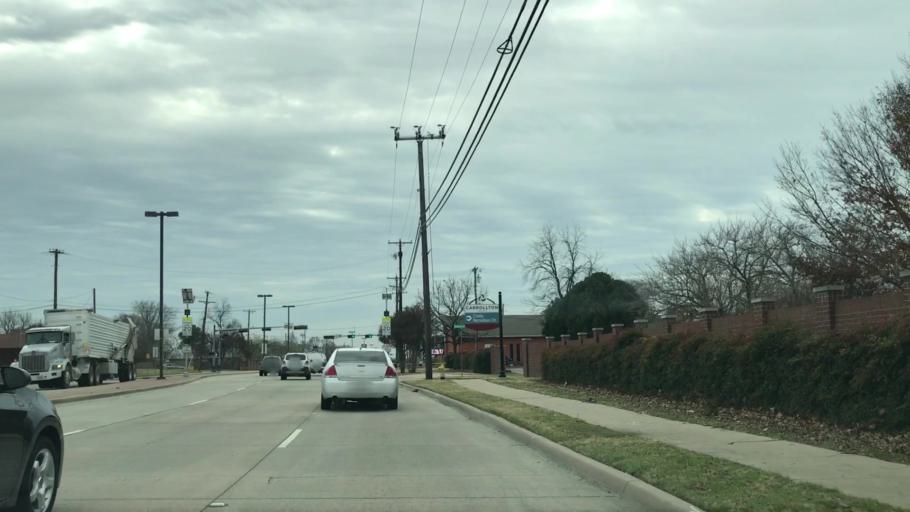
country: US
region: Texas
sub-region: Dallas County
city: Carrollton
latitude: 32.9505
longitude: -96.8905
